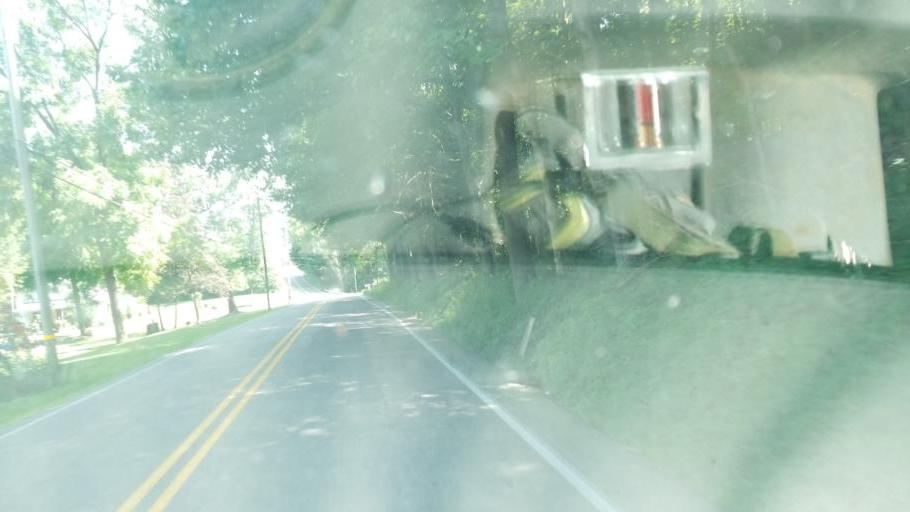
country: US
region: Pennsylvania
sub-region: Clarion County
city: Knox
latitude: 41.1725
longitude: -79.6963
